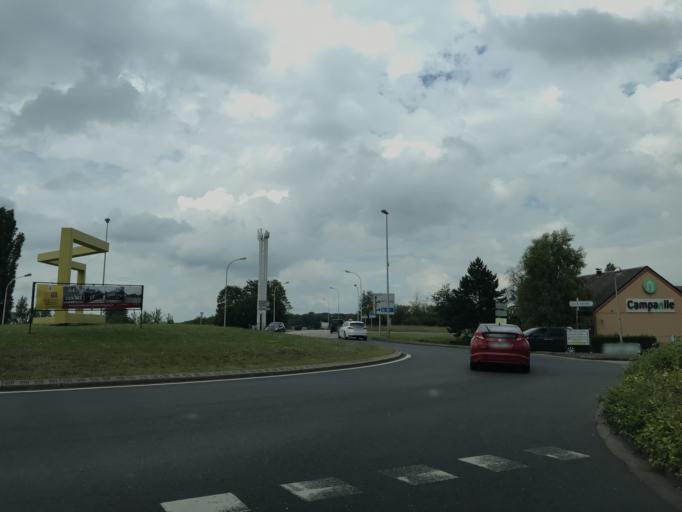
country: FR
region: Haute-Normandie
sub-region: Departement de la Seine-Maritime
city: Mont-Saint-Aignan
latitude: 49.4765
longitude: 1.0929
